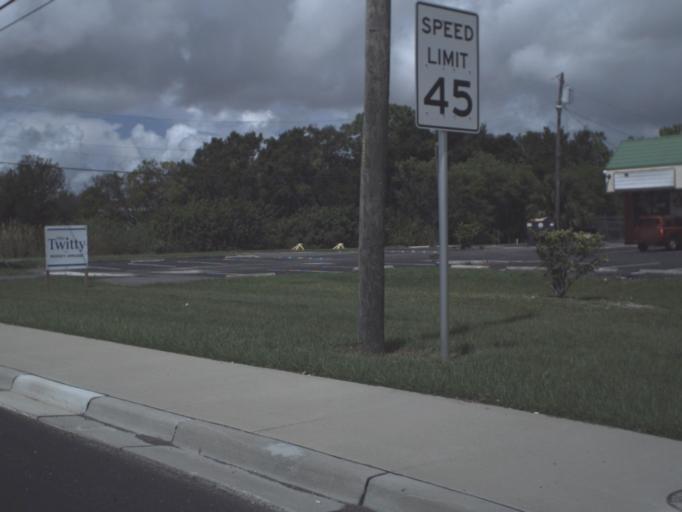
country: US
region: Florida
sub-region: Pinellas County
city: Largo
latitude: 27.8946
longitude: -82.7646
